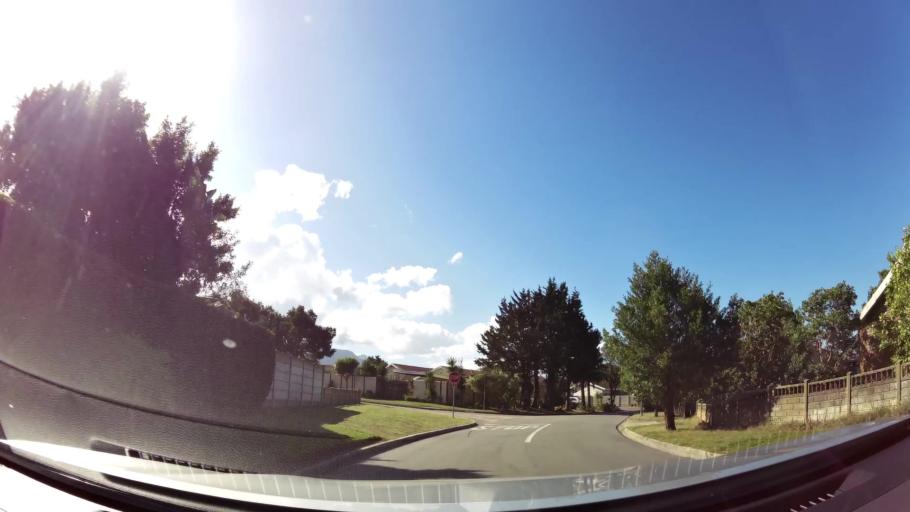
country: ZA
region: Western Cape
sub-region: Eden District Municipality
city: George
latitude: -33.9774
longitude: 22.4439
